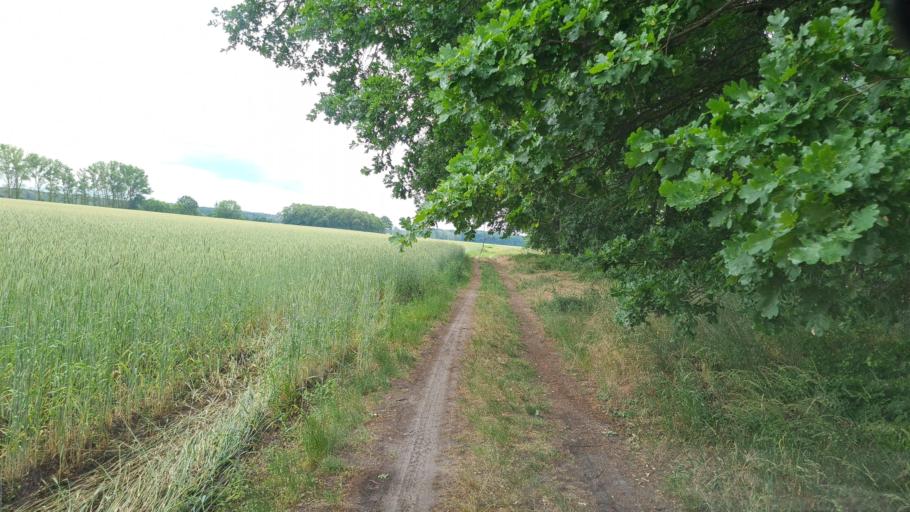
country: DE
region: Brandenburg
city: Bronkow
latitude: 51.6295
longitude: 13.9332
